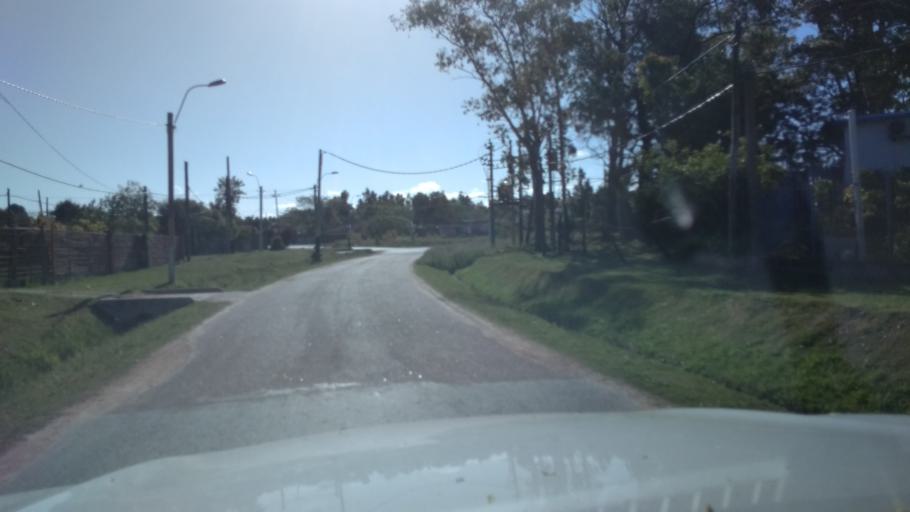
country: UY
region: Canelones
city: Colonia Nicolich
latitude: -34.8304
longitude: -55.9807
